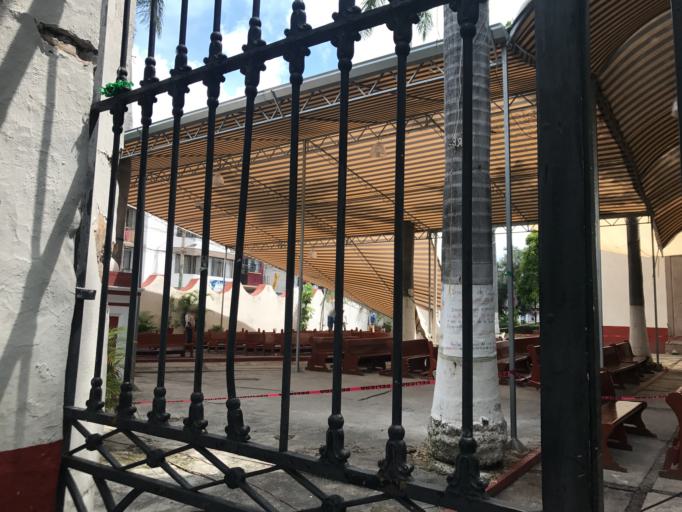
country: MX
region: Morelos
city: Cuautla Morelos
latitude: 18.8105
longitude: -98.9553
